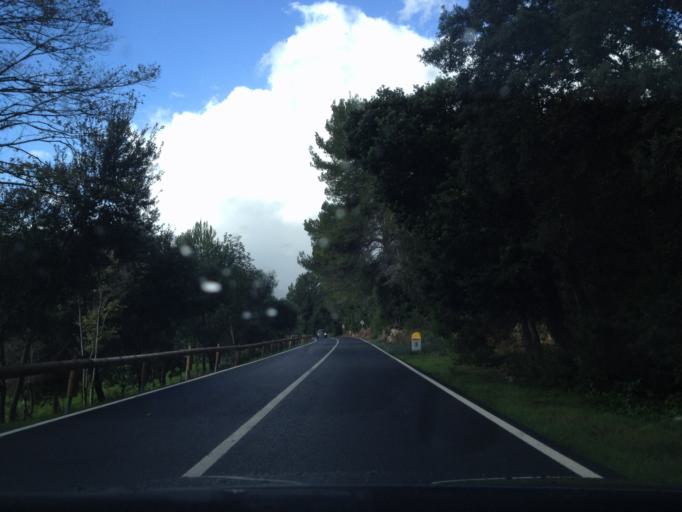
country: ES
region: Balearic Islands
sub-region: Illes Balears
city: Pollenca
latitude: 39.8745
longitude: 2.9916
